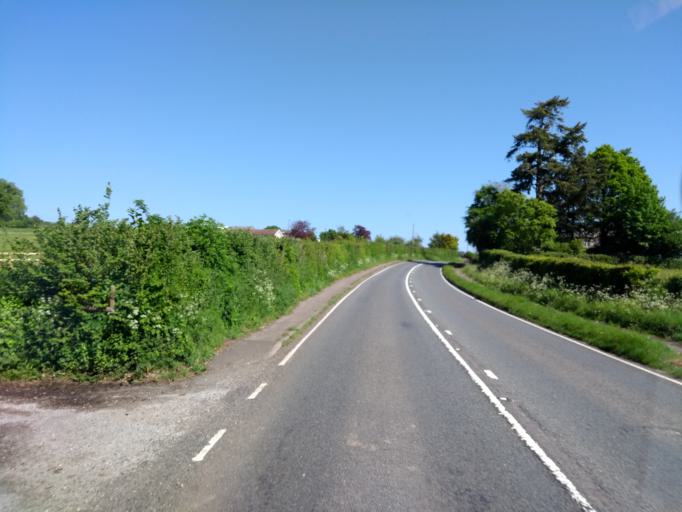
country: GB
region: England
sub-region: Somerset
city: Chard
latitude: 50.8504
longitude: -2.9576
